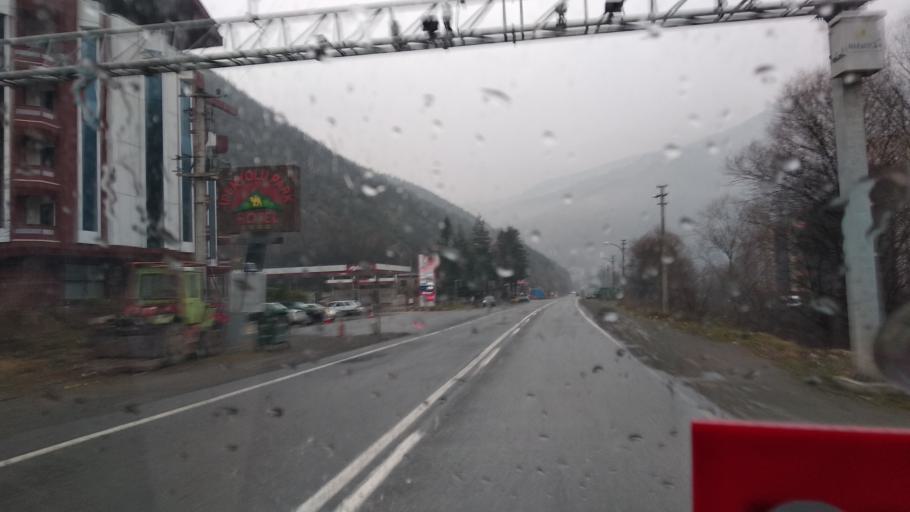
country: TR
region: Trabzon
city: Macka
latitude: 40.8081
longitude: 39.6000
